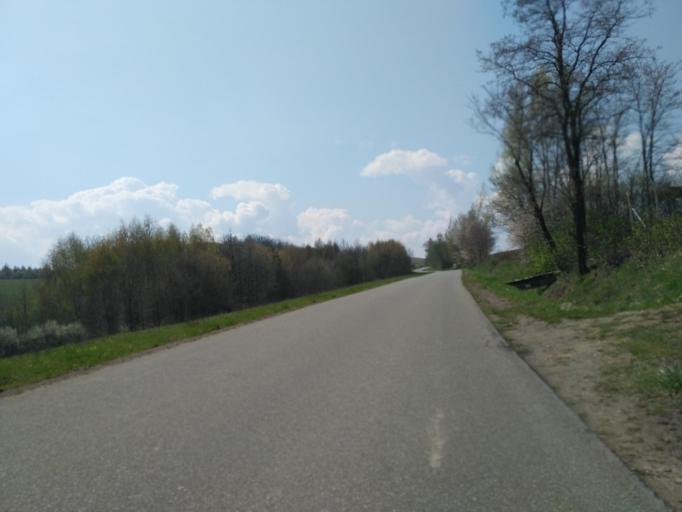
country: PL
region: Subcarpathian Voivodeship
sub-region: Powiat sanocki
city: Zarszyn
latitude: 49.5696
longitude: 22.0044
